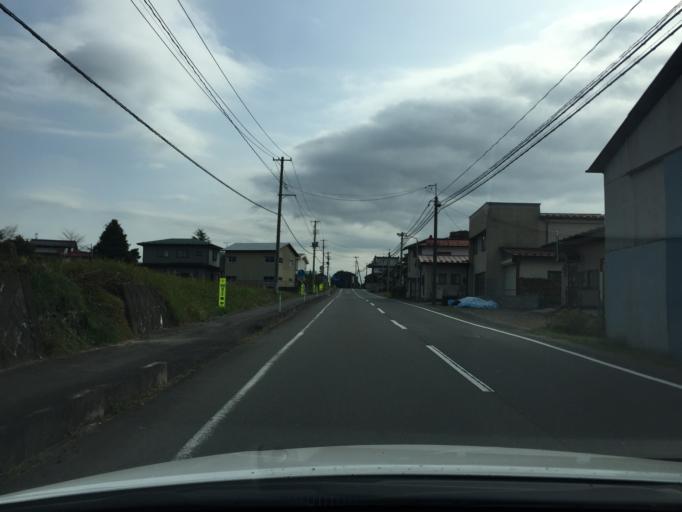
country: JP
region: Fukushima
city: Ishikawa
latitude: 36.9695
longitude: 140.4325
